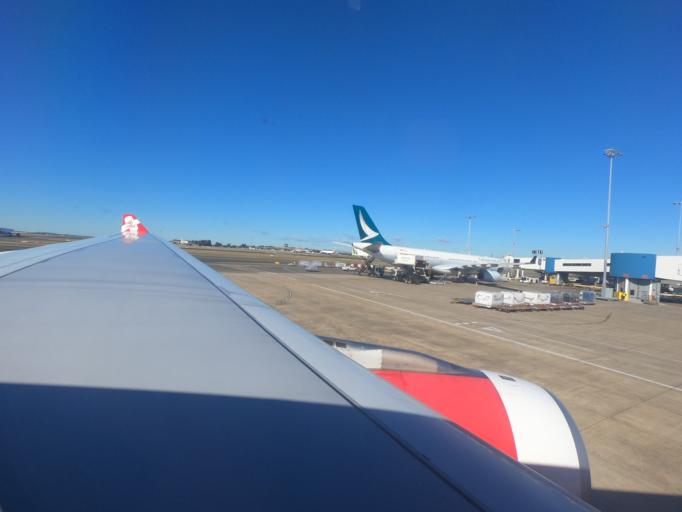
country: AU
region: New South Wales
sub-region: Rockdale
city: Arncliffe
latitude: -33.9385
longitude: 151.1705
